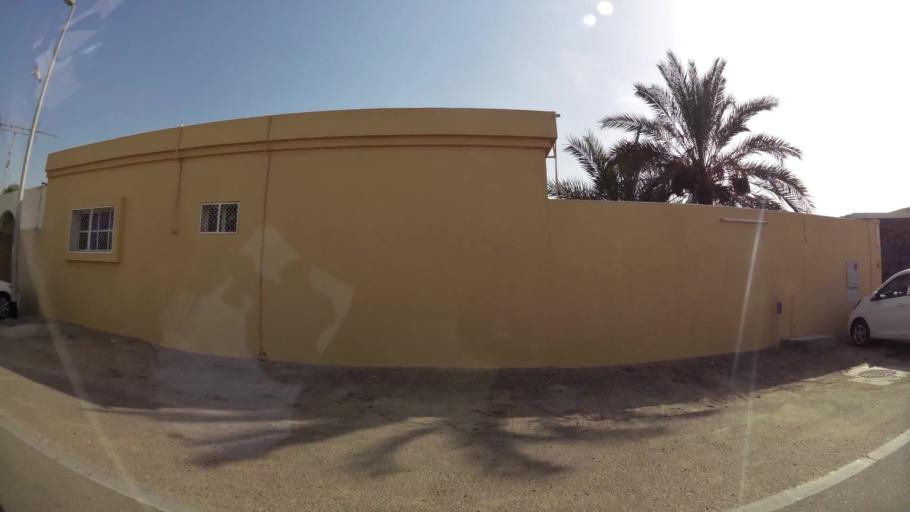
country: AE
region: Ash Shariqah
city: Sharjah
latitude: 25.2189
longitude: 55.3994
